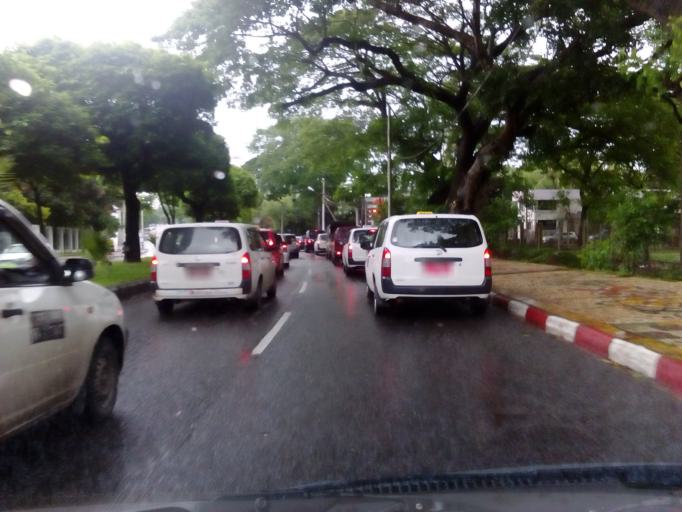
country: MM
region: Yangon
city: Yangon
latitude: 16.8021
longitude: 96.1443
